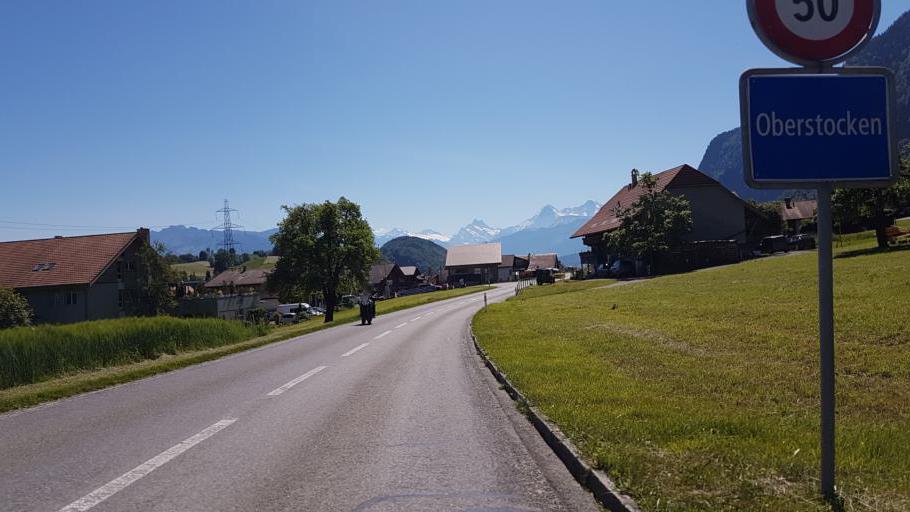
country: CH
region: Bern
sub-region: Thun District
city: Blumenstein
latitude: 46.7180
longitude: 7.5523
